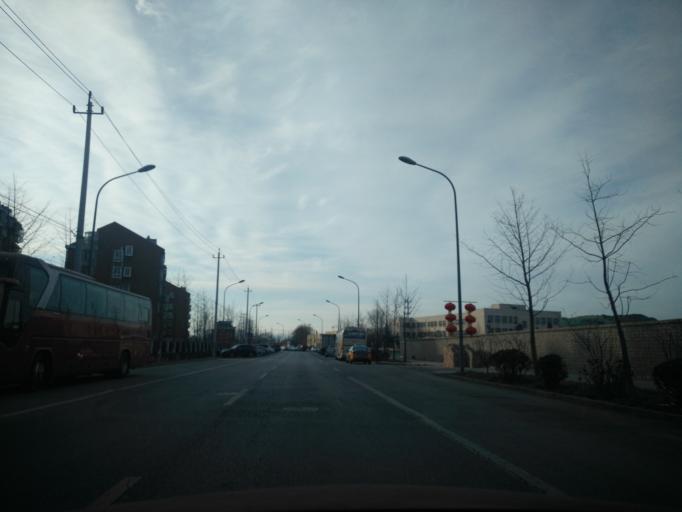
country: CN
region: Beijing
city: Nanyuan
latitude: 39.8162
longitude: 116.3689
